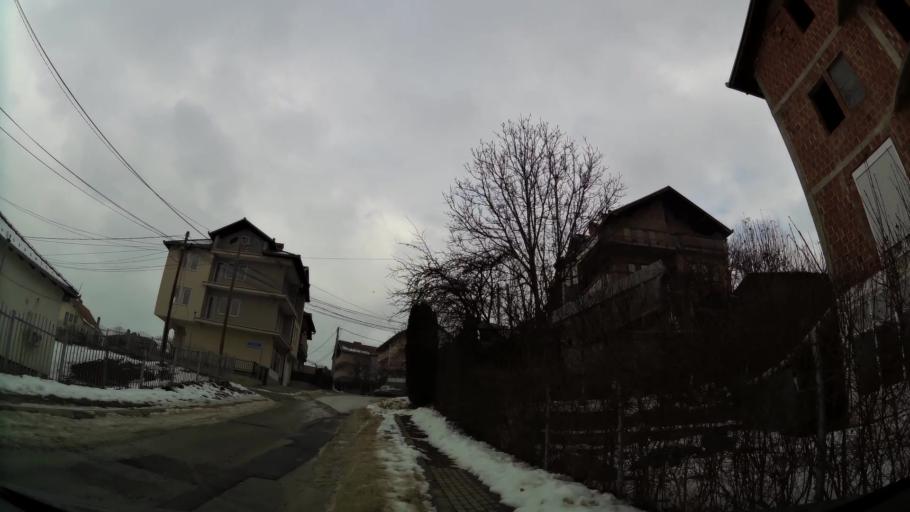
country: XK
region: Pristina
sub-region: Komuna e Prishtines
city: Pristina
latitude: 42.6788
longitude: 21.1790
